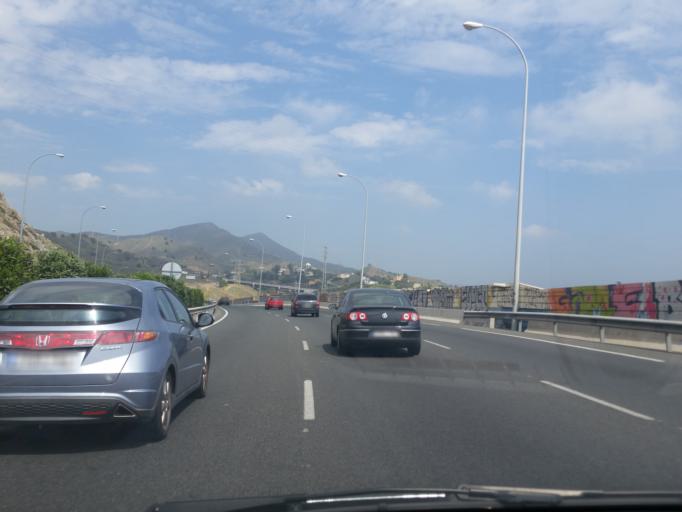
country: ES
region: Andalusia
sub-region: Provincia de Malaga
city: Malaga
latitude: 36.7343
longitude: -4.4540
